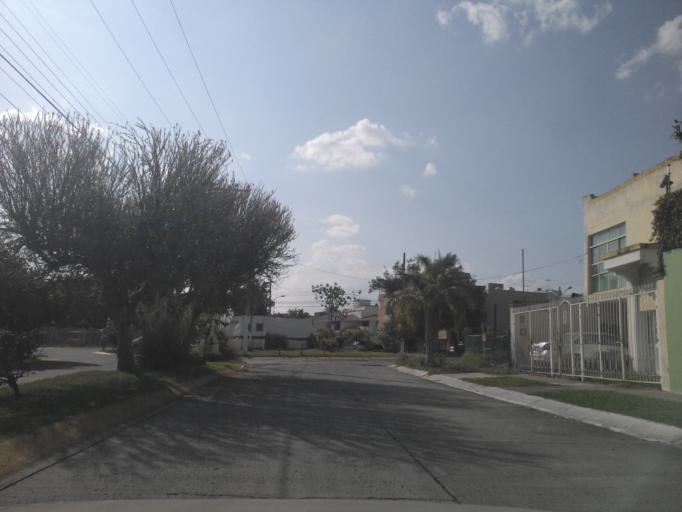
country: MX
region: Jalisco
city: Guadalajara
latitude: 20.6571
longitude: -103.4119
